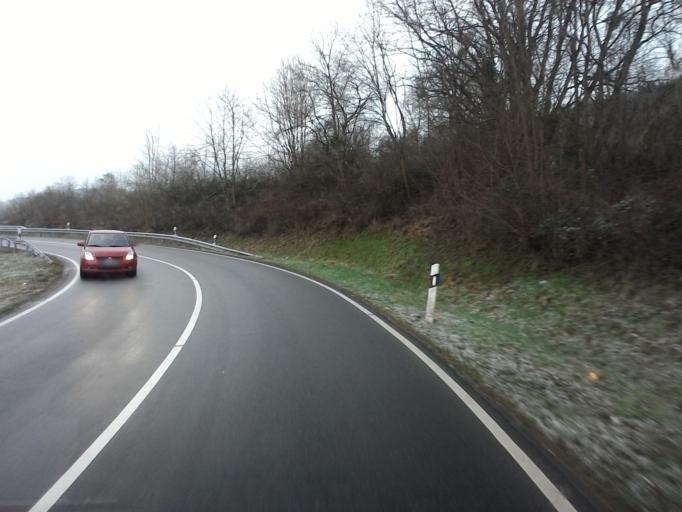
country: DE
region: Rheinland-Pfalz
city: Irrel
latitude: 49.8527
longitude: 6.4579
